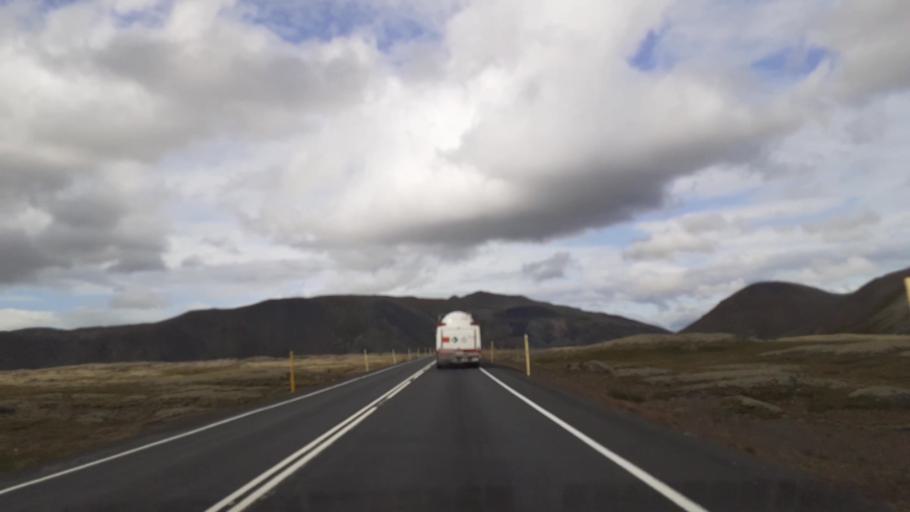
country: IS
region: South
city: THorlakshoefn
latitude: 63.9899
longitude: -21.4629
